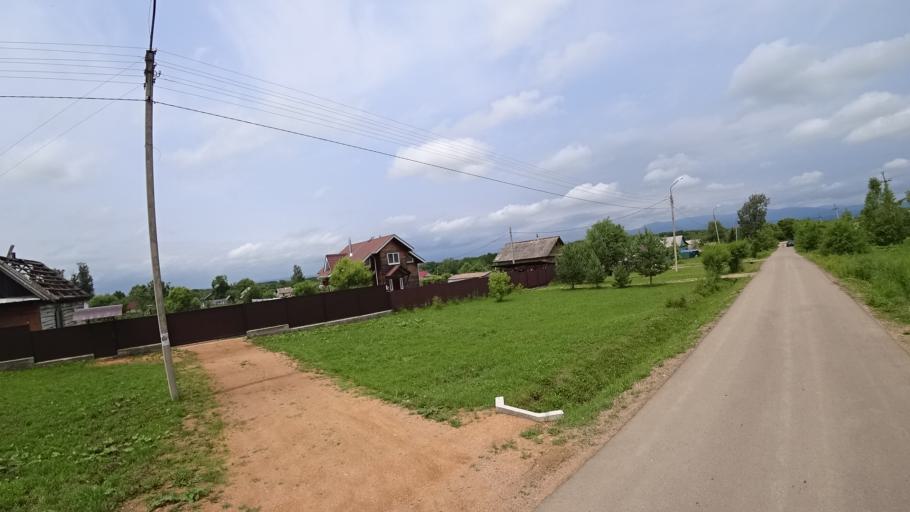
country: RU
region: Primorskiy
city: Novosysoyevka
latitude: 44.2367
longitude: 133.3586
